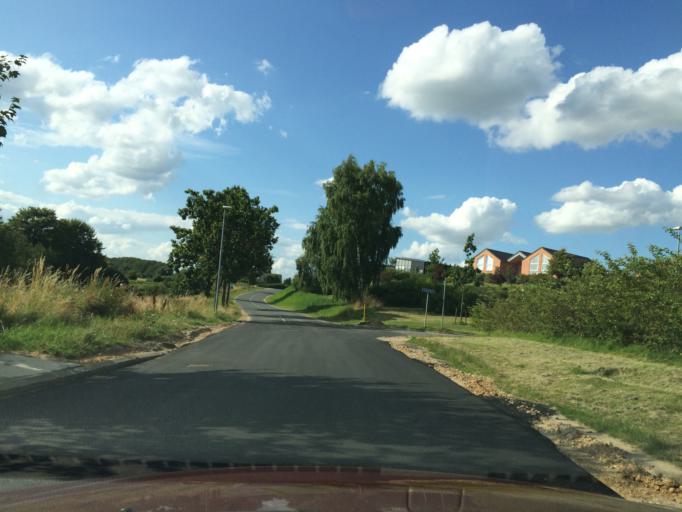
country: DK
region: Central Jutland
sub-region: Favrskov Kommune
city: Hammel
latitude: 56.2341
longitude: 9.7417
